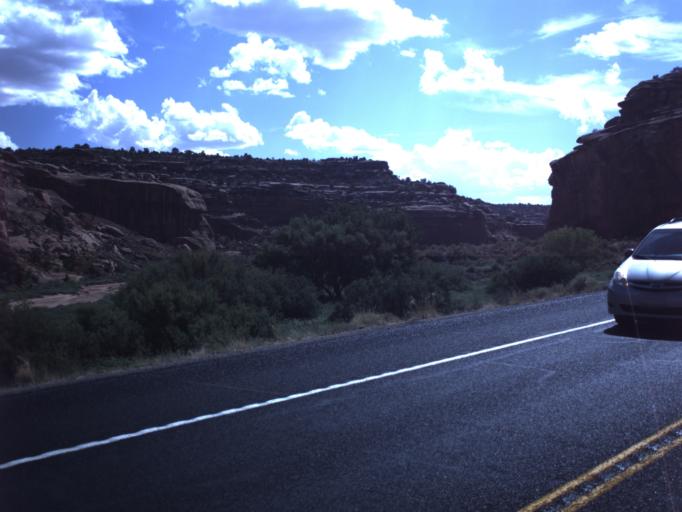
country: US
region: Utah
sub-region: Grand County
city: Moab
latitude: 38.6491
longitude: -109.7224
